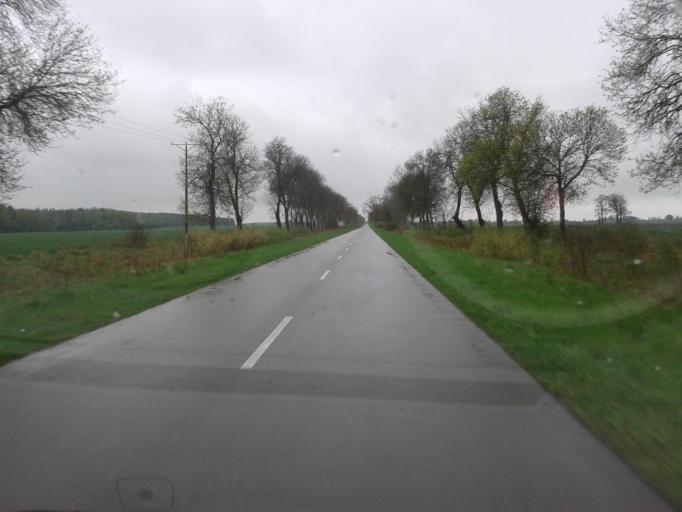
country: UA
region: Lviv
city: Uhniv
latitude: 50.4142
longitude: 23.7425
